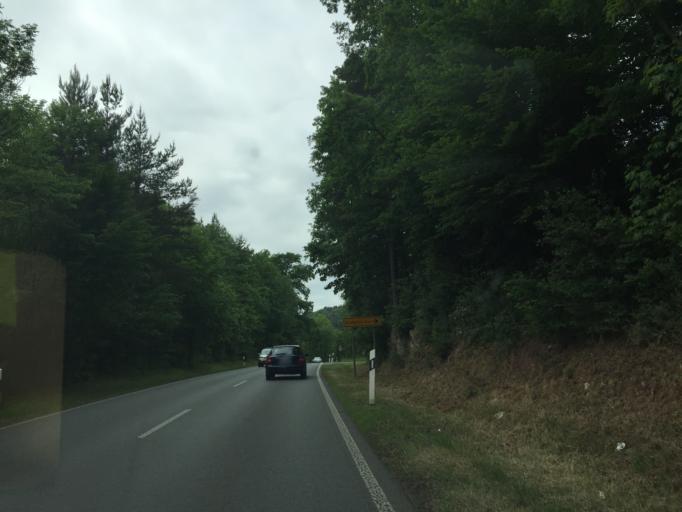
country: DE
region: Thuringia
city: Bad Blankenburg
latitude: 50.6942
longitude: 11.2282
